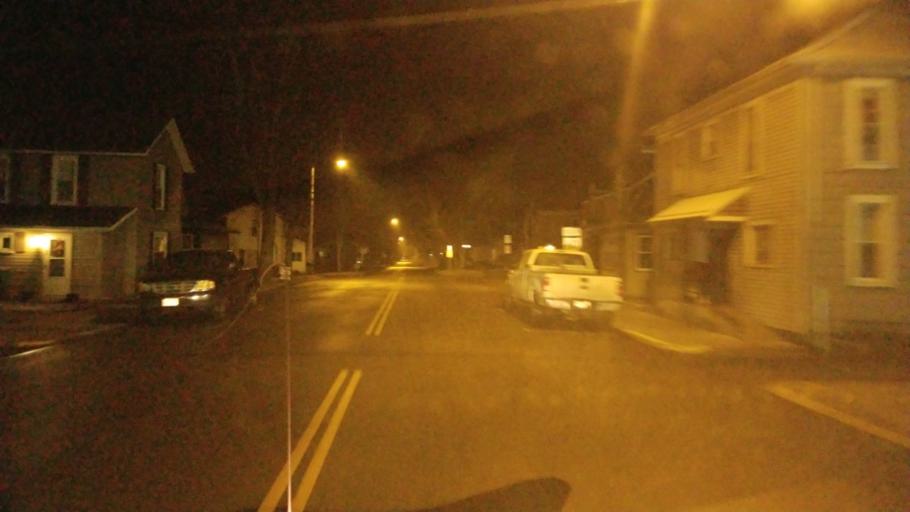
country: US
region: Ohio
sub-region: Holmes County
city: Millersburg
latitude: 40.4948
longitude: -81.9843
